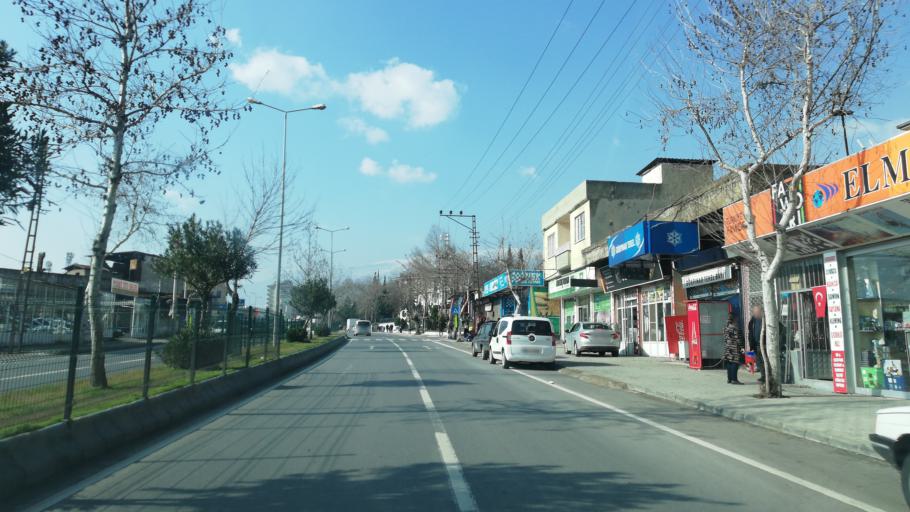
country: TR
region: Kahramanmaras
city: Kahramanmaras
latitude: 37.5696
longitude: 36.9462
